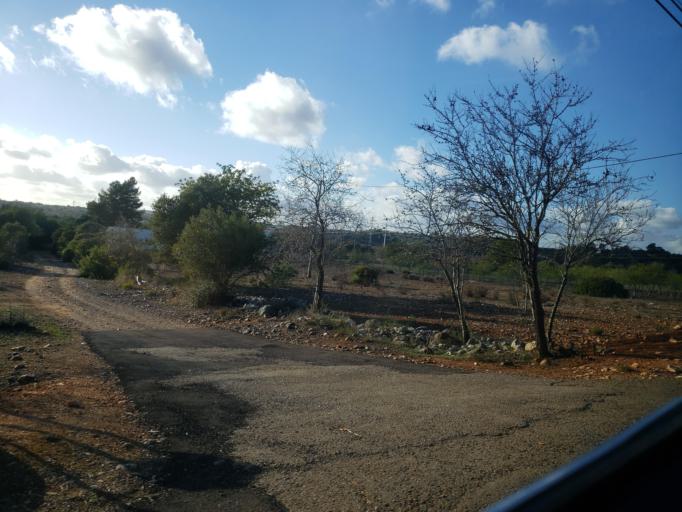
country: PT
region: Faro
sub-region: Portimao
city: Alvor
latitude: 37.1867
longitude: -8.5872
